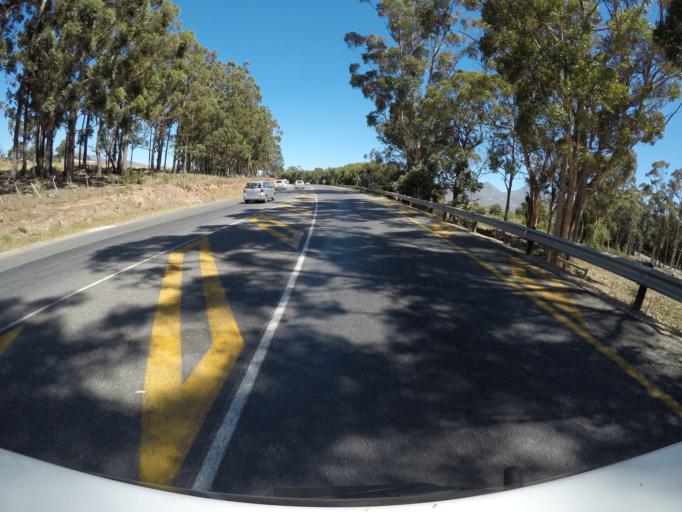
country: ZA
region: Western Cape
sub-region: Overberg District Municipality
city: Grabouw
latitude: -34.1629
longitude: 19.0336
